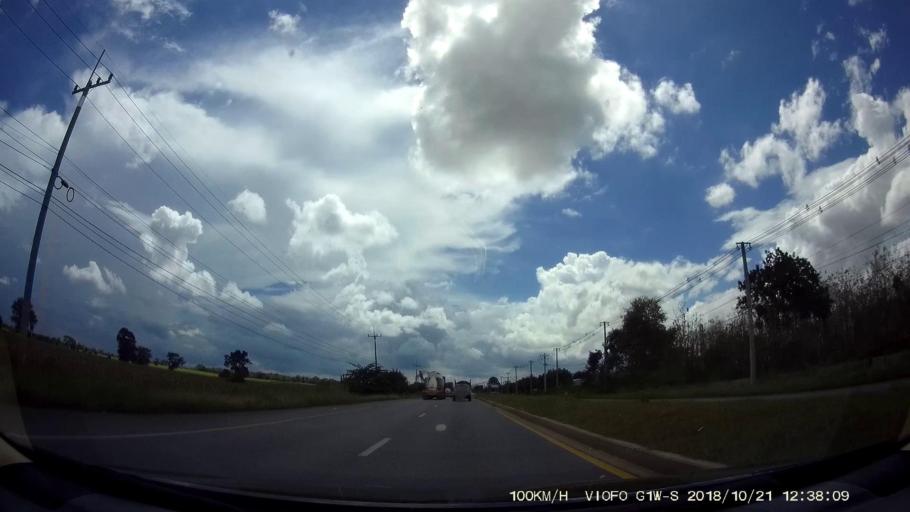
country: TH
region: Nakhon Ratchasima
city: Amphoe Sikhiu
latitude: 15.0582
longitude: 101.7076
